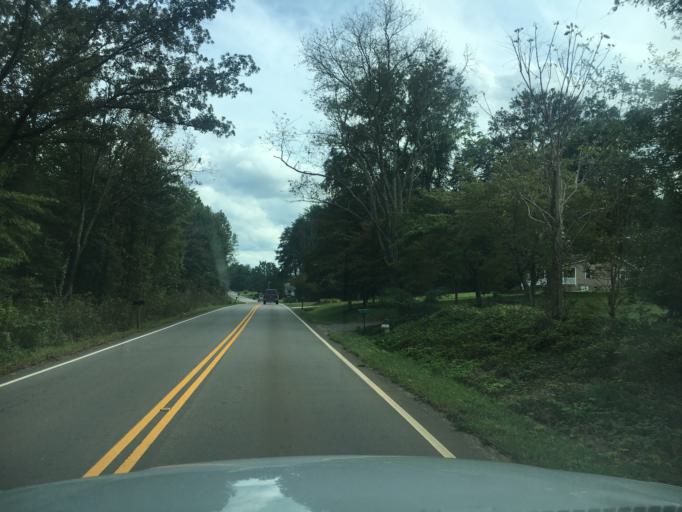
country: US
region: South Carolina
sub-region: Spartanburg County
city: Wellford
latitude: 34.9181
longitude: -82.0607
